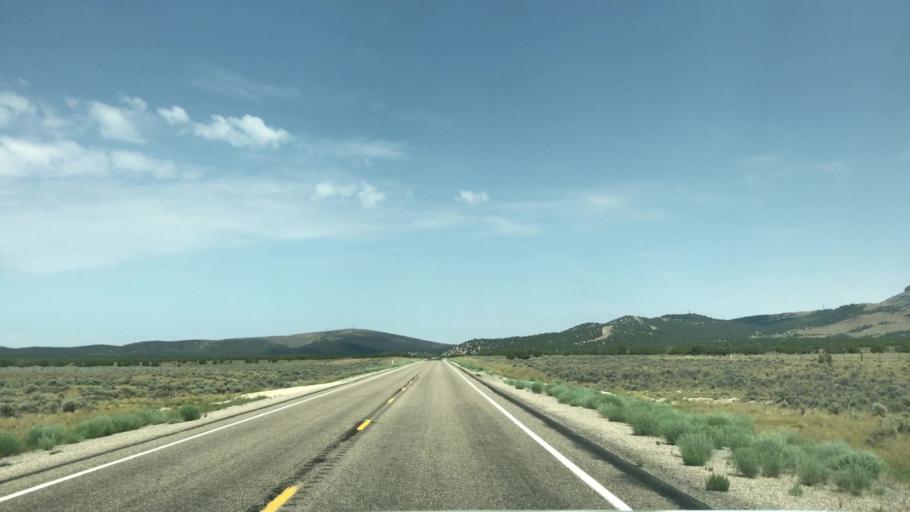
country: US
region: Nevada
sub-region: White Pine County
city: Ely
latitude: 39.3659
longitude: -115.0527
